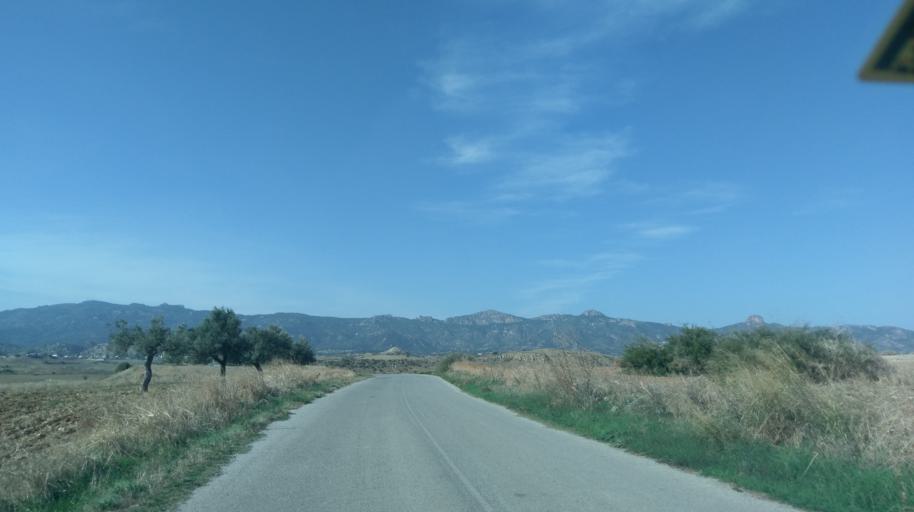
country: CY
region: Ammochostos
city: Trikomo
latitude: 35.3583
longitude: 33.9565
